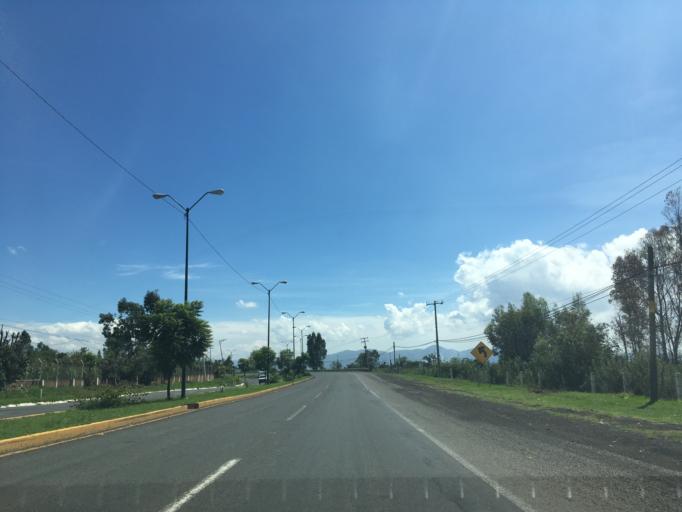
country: MX
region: Michoacan
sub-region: Morelia
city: Lomas de la Maestranza
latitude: 19.6843
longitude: -101.3361
